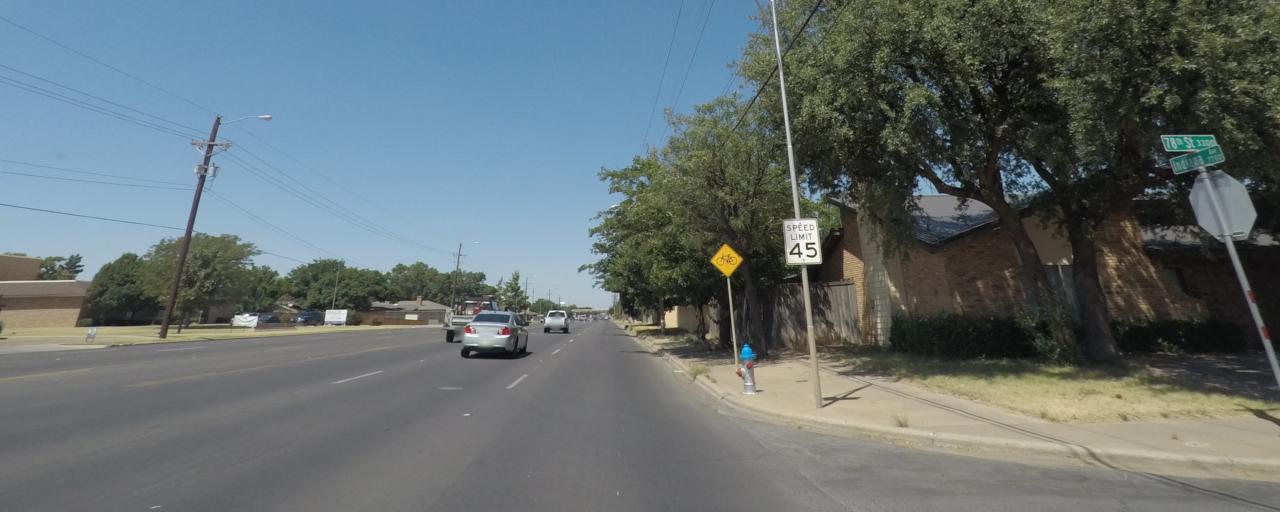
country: US
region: Texas
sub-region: Lubbock County
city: Lubbock
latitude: 33.5234
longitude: -101.8876
